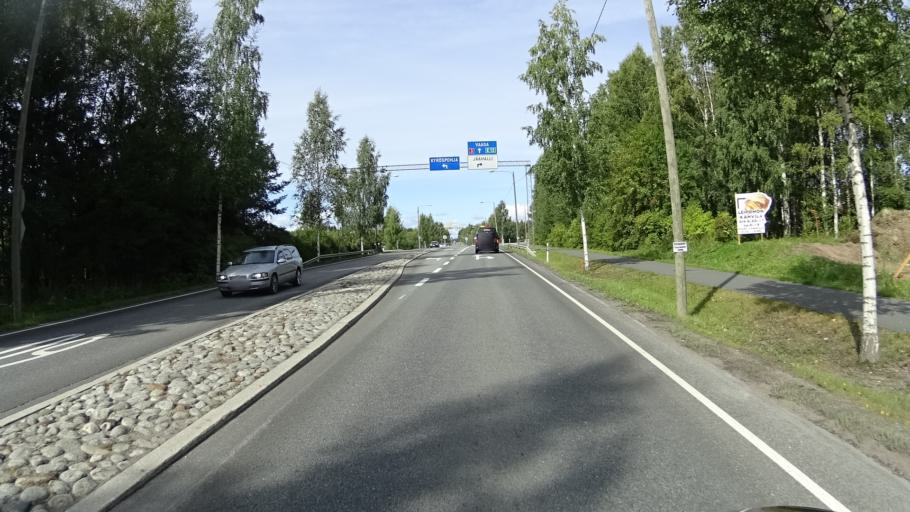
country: FI
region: Pirkanmaa
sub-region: Tampere
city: Haemeenkyroe
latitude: 61.6436
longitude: 23.1896
